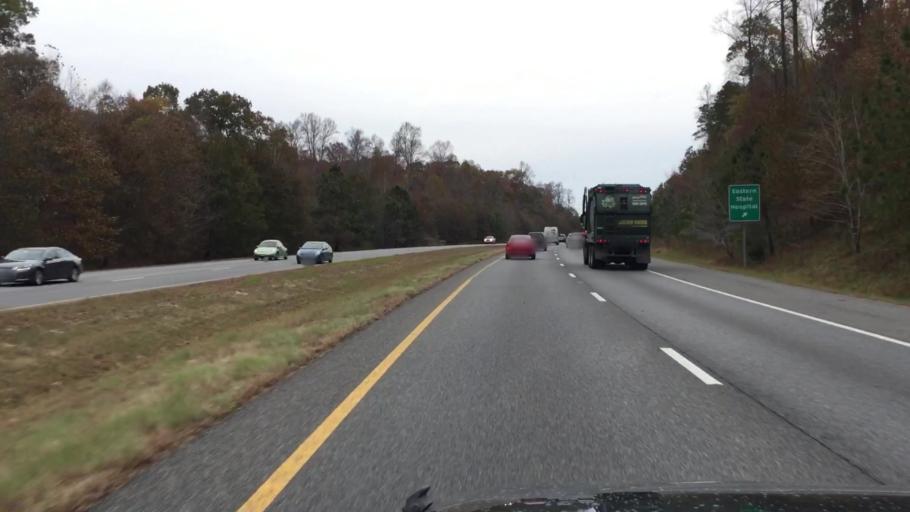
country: US
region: Virginia
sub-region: James City County
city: Williamsburg
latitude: 37.2936
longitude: -76.7511
